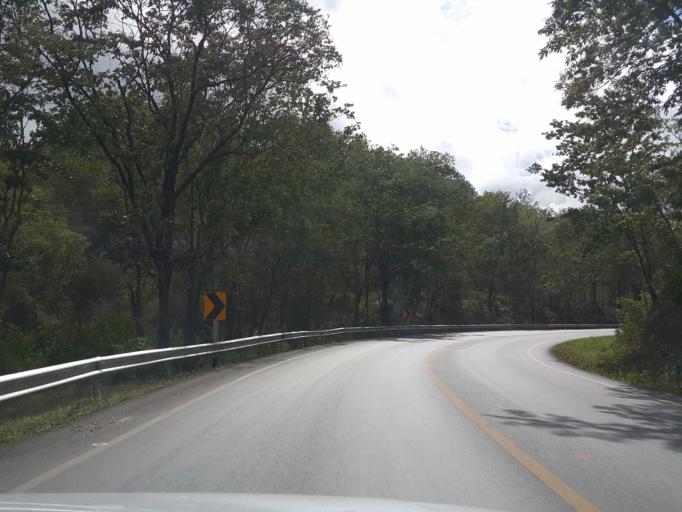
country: TH
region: Tak
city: Tak
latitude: 16.8090
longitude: 98.9917
